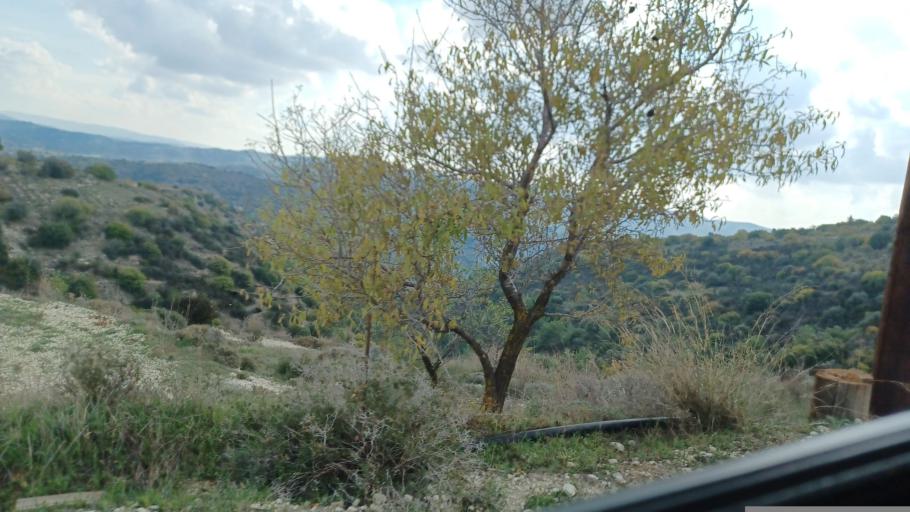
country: CY
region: Pafos
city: Mesogi
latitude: 34.8316
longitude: 32.5244
